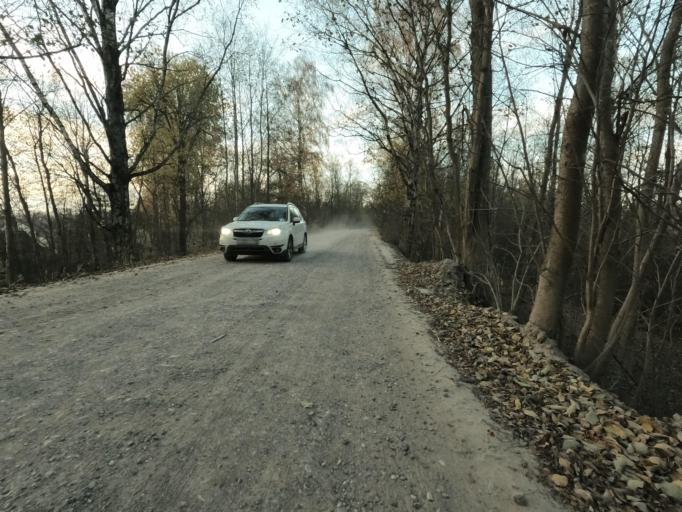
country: RU
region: Leningrad
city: Mga
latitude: 59.7711
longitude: 31.2278
